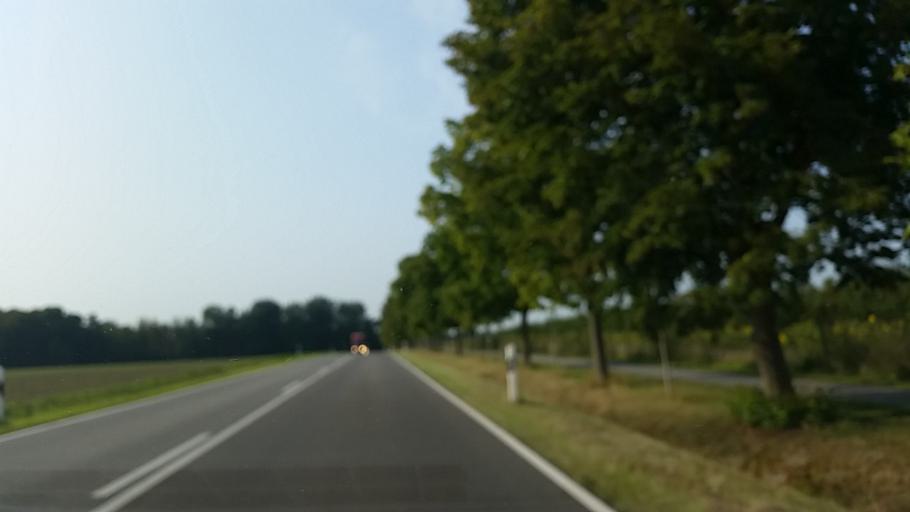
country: DE
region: Mecklenburg-Vorpommern
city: Lubtheen
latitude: 53.3861
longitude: 11.0866
